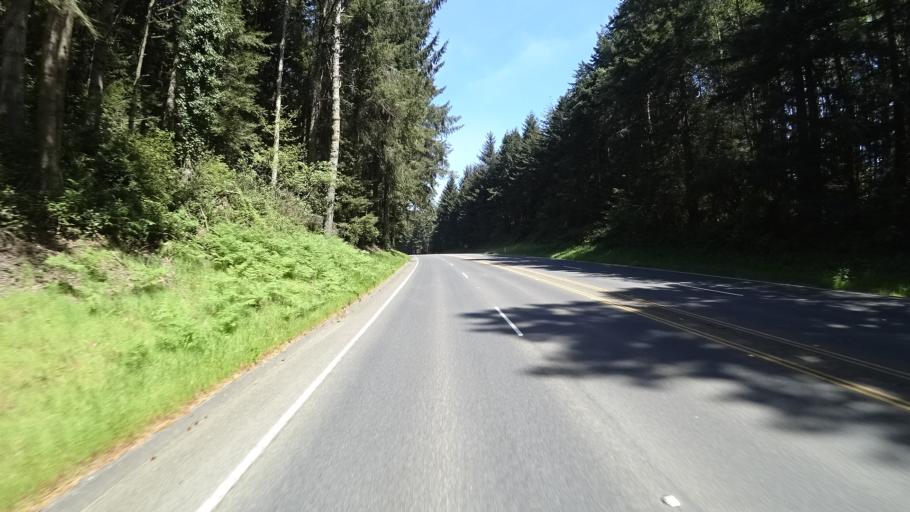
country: US
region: California
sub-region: Humboldt County
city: Westhaven-Moonstone
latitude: 41.1418
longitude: -124.1369
